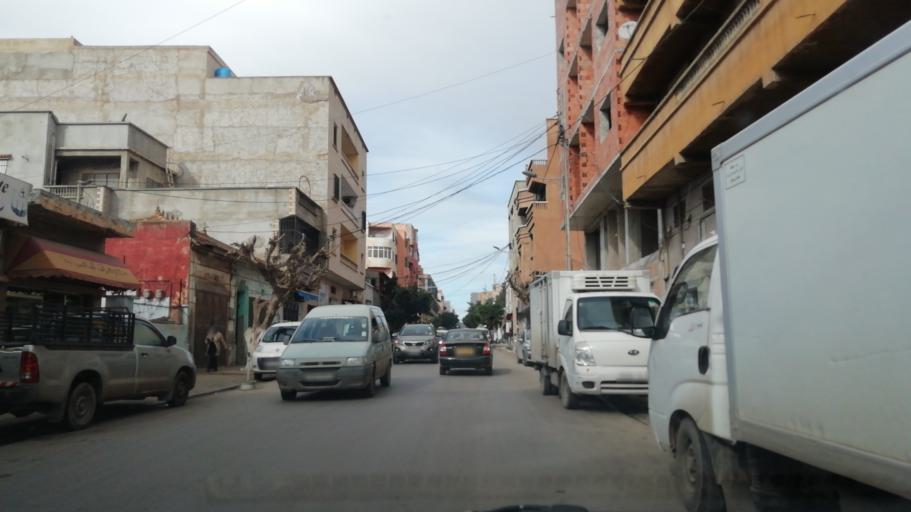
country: DZ
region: Oran
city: Oran
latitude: 35.6847
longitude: -0.6156
